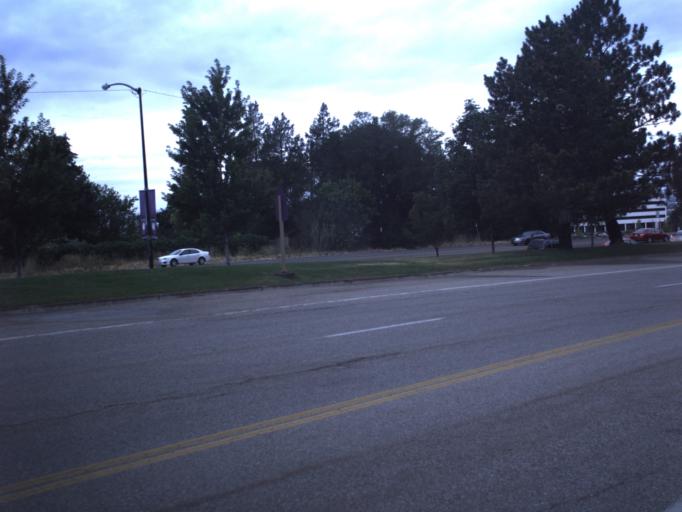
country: US
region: Utah
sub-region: Weber County
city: South Ogden
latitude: 41.1887
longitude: -111.9482
